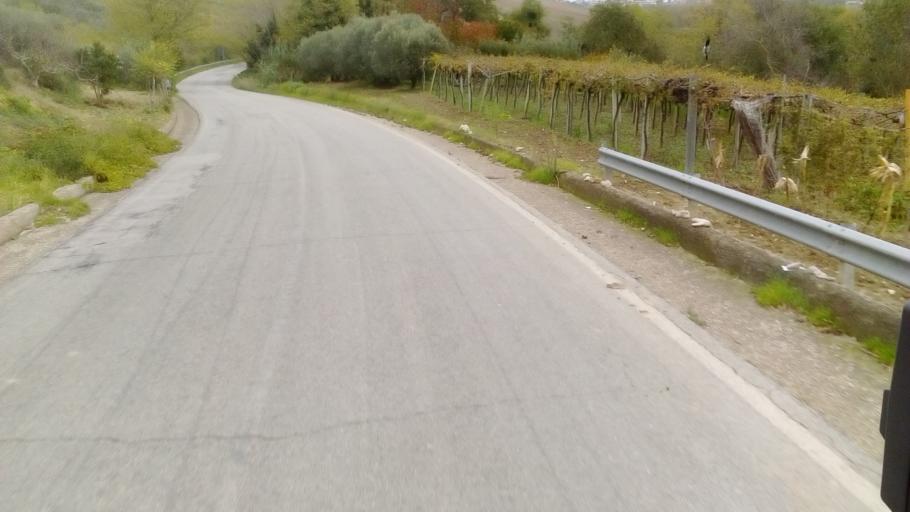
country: IT
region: Abruzzo
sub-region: Provincia di Chieti
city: San Salvo
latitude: 42.0576
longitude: 14.7179
